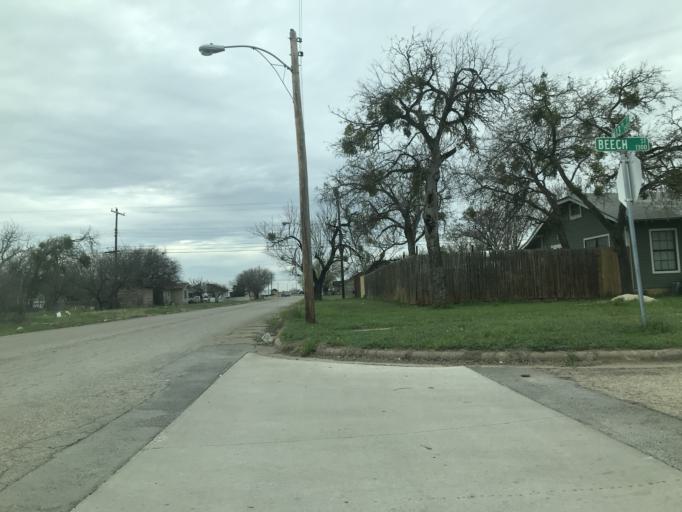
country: US
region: Texas
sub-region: Taylor County
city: Abilene
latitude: 32.4638
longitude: -99.7378
